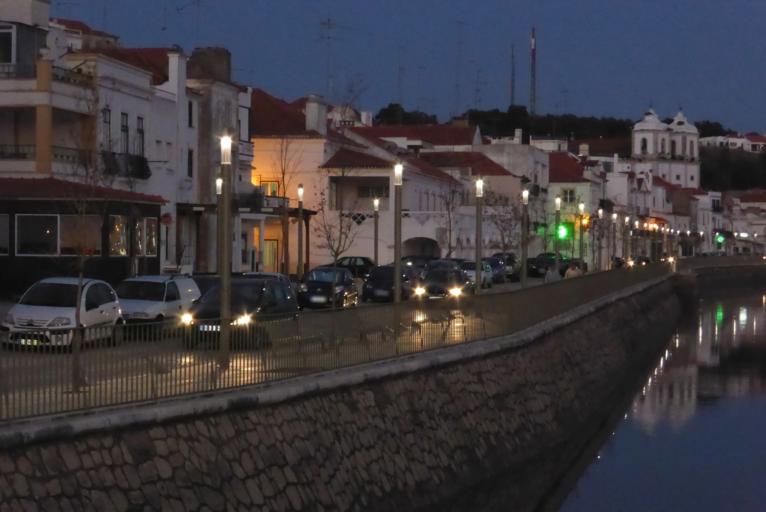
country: PT
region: Setubal
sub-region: Alcacer do Sal
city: Alcacer do Sal
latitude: 38.3704
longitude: -8.5130
